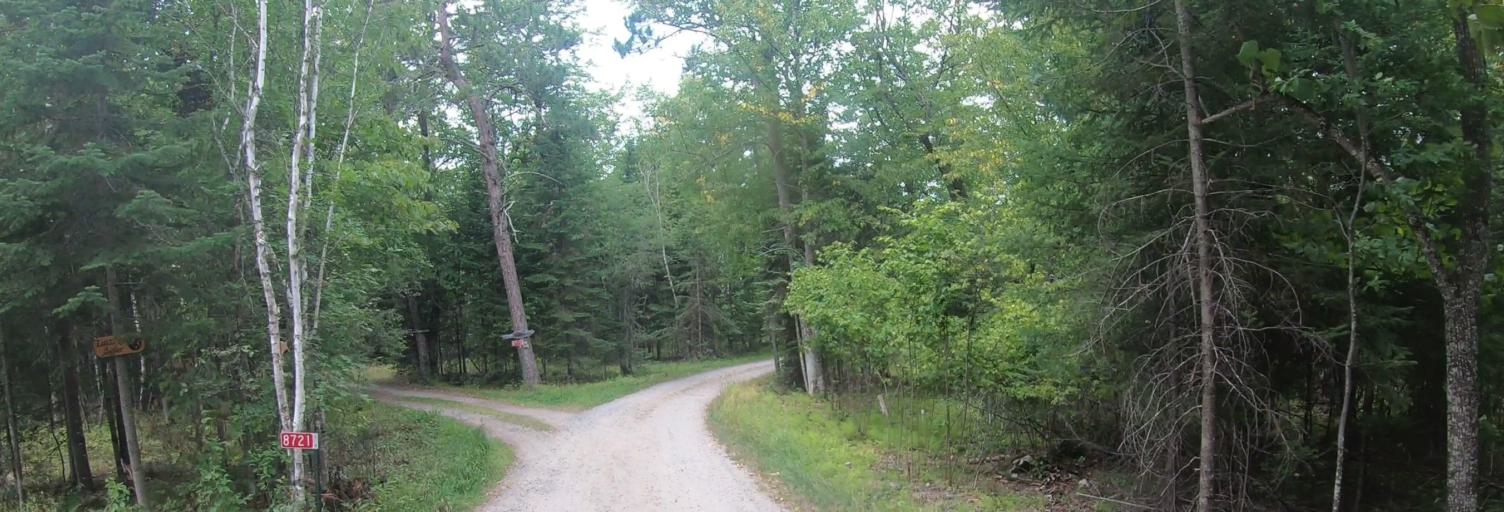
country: US
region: Minnesota
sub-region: Saint Louis County
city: Mountain Iron
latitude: 47.9429
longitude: -92.6295
